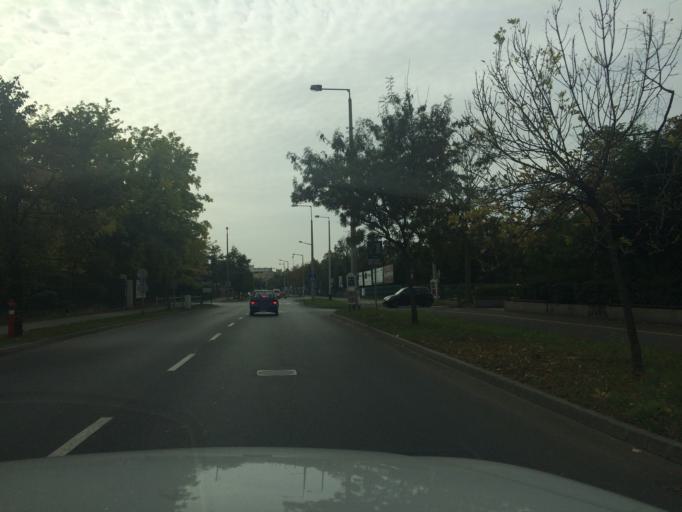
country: HU
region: Szabolcs-Szatmar-Bereg
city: Nyiregyhaza
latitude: 47.9720
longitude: 21.7160
